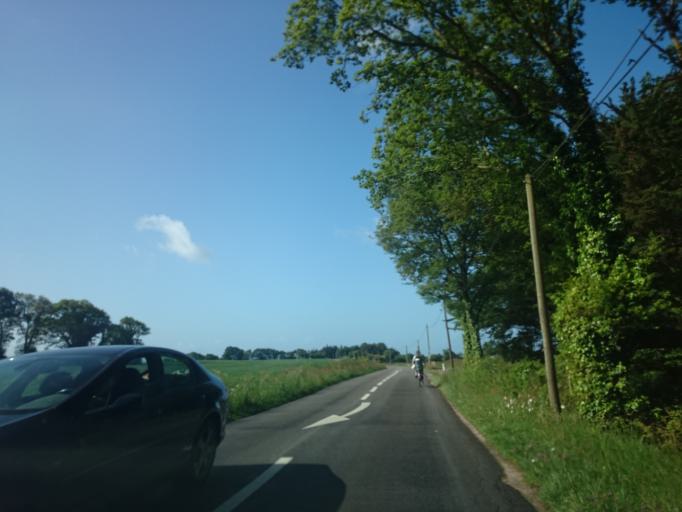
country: FR
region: Brittany
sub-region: Departement du Morbihan
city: Larmor-Baden
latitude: 47.6101
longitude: -2.8885
